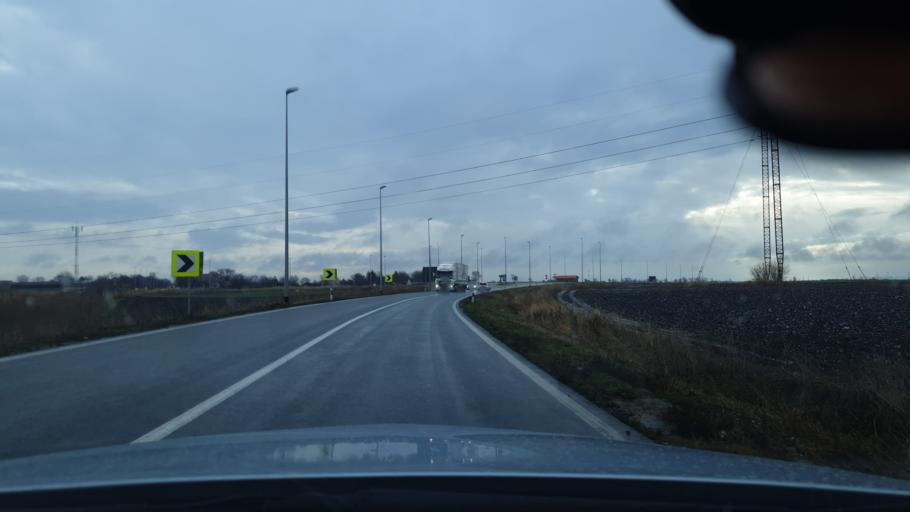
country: RS
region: Autonomna Pokrajina Vojvodina
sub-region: Juznobanatski Okrug
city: Kovin
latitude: 44.8254
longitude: 20.8498
